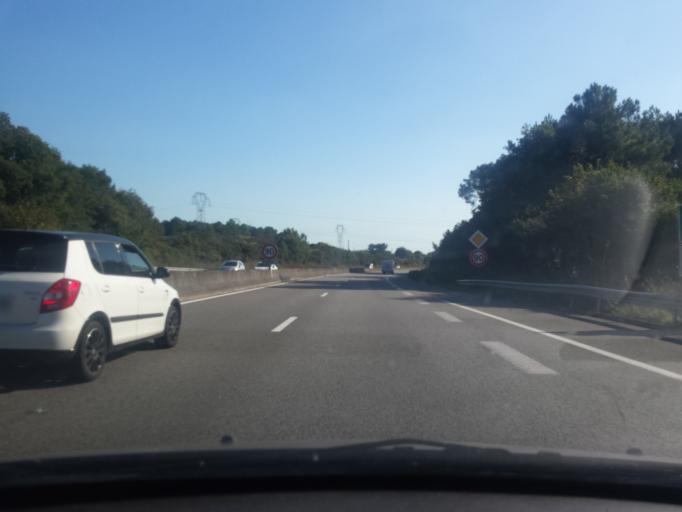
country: FR
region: Brittany
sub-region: Departement du Morbihan
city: Saint-Ave
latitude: 47.6950
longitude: -2.7650
